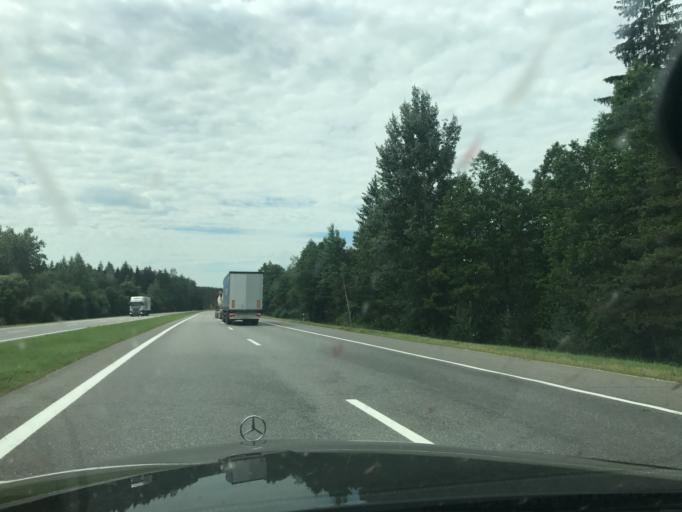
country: BY
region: Minsk
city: Zamostochcha
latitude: 53.8739
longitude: 27.9268
